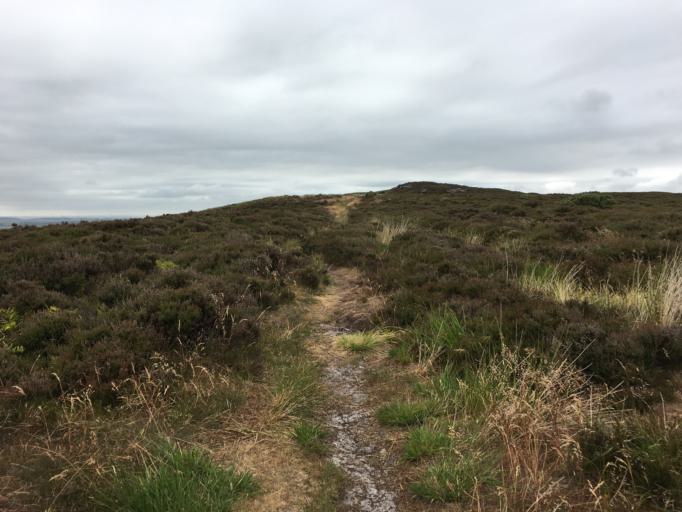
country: GB
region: England
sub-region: Northumberland
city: Lowick
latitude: 55.6134
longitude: -1.9094
